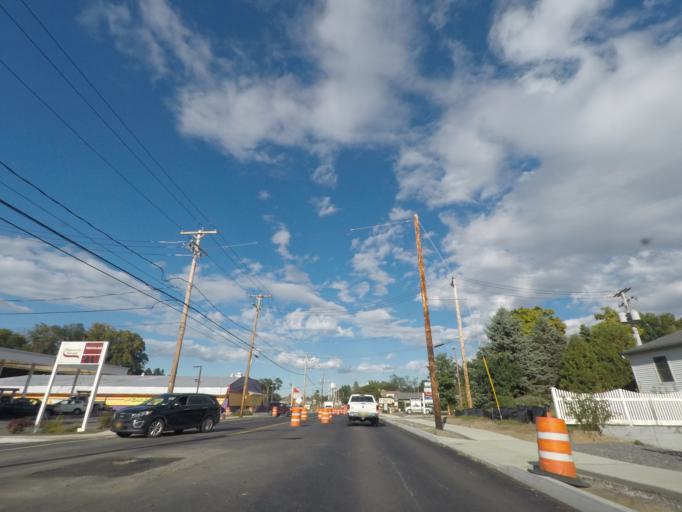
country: US
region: New York
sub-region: Schenectady County
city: Rotterdam
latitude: 42.7734
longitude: -73.9358
